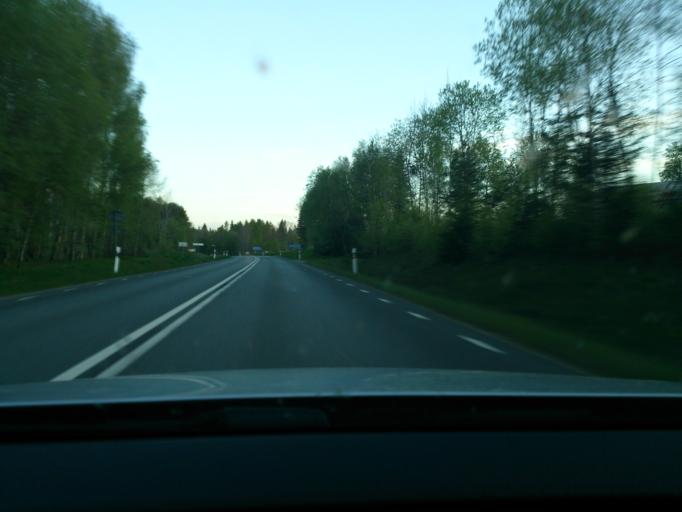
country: SE
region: Kronoberg
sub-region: Alvesta Kommun
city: Moheda
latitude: 57.0376
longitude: 14.5645
